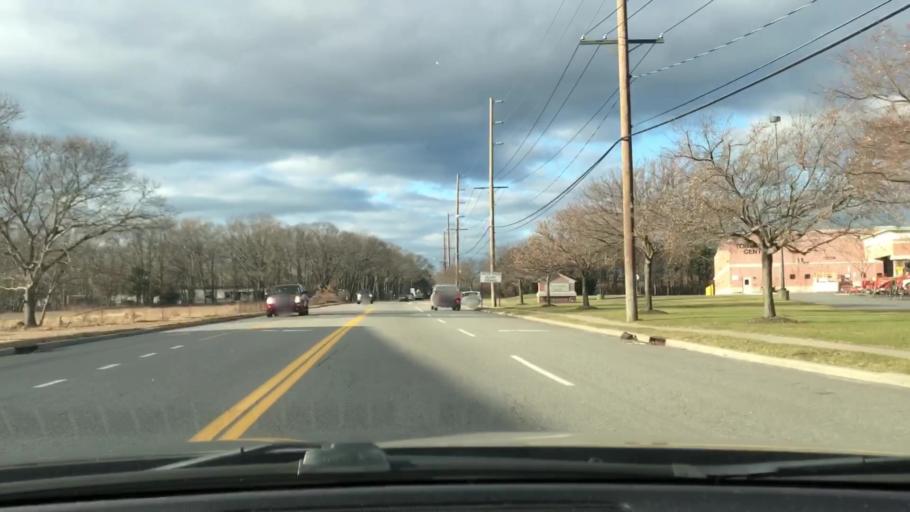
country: US
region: New York
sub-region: Suffolk County
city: Riverhead
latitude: 40.9266
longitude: -72.6981
